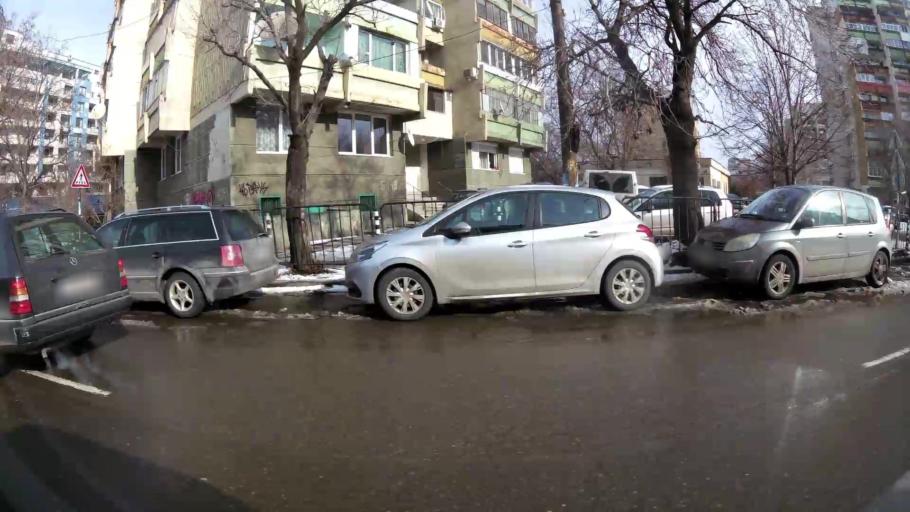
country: BG
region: Sofia-Capital
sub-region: Stolichna Obshtina
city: Sofia
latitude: 42.7089
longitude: 23.3565
